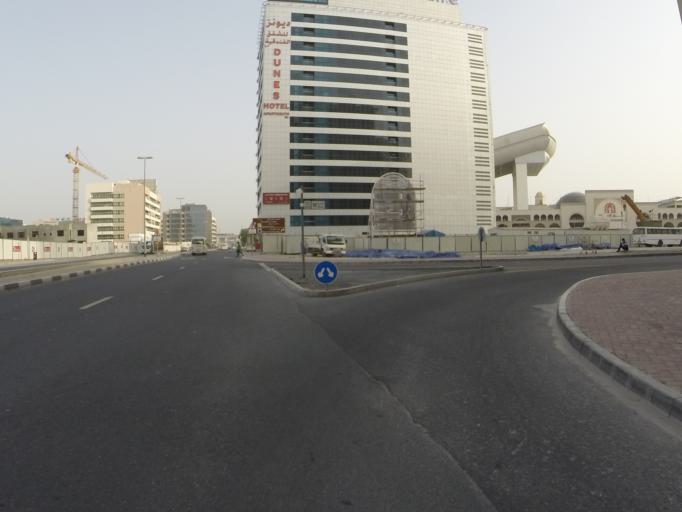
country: AE
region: Dubai
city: Dubai
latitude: 25.1139
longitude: 55.1999
